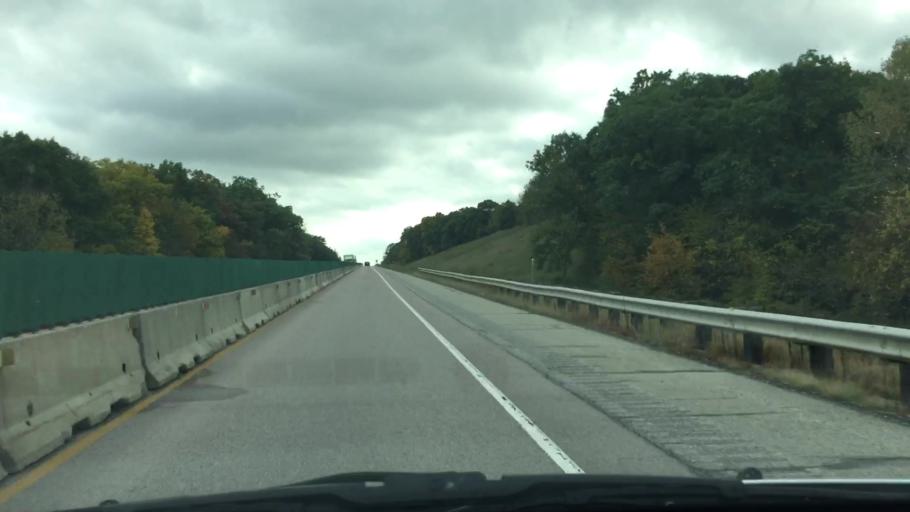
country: US
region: Iowa
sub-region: Decatur County
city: Leon
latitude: 40.7102
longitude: -93.8456
